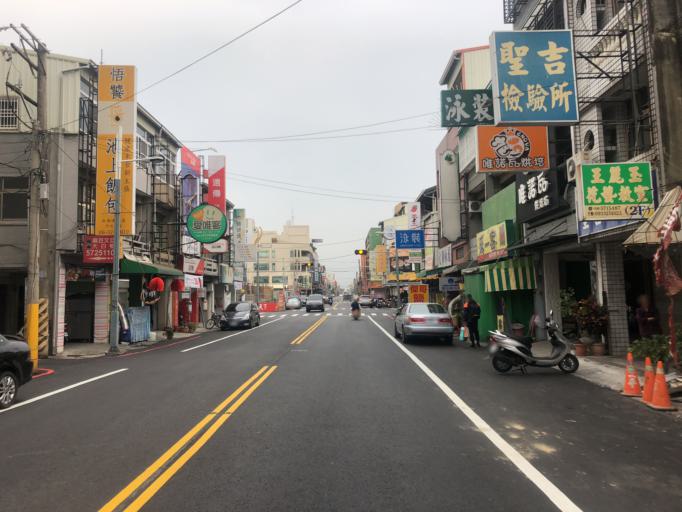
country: TW
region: Taiwan
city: Xinying
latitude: 23.1838
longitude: 120.2526
